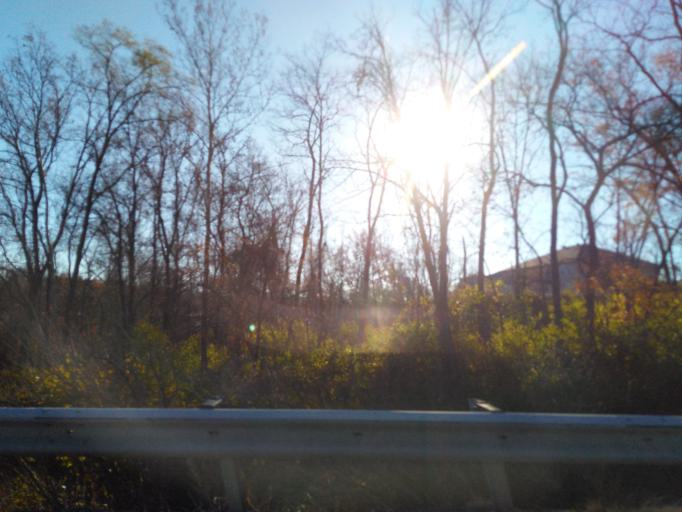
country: US
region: Illinois
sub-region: Madison County
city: Collinsville
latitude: 38.6859
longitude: -90.0058
